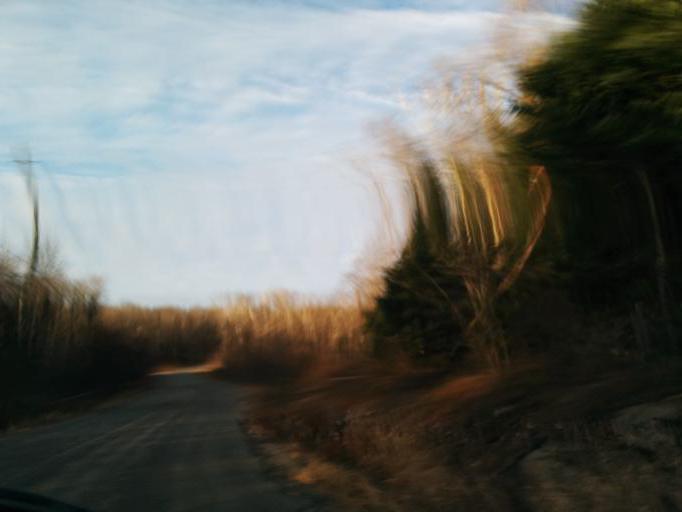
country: CA
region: Ontario
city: Bancroft
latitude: 45.0518
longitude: -78.5343
